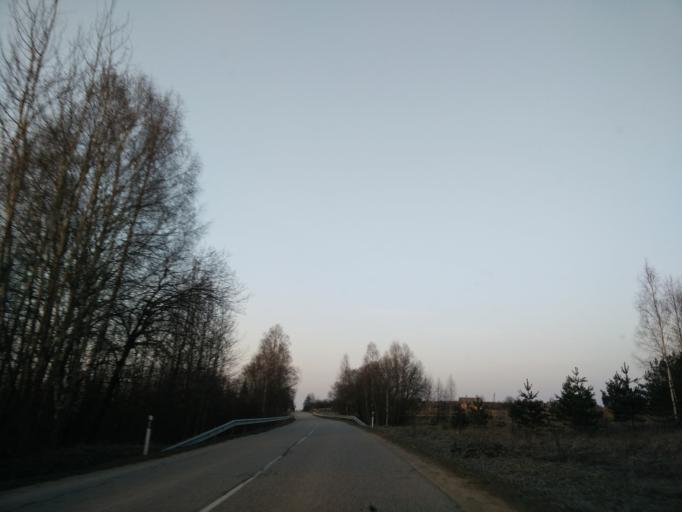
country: LT
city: Trakai
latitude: 54.6856
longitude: 24.9572
